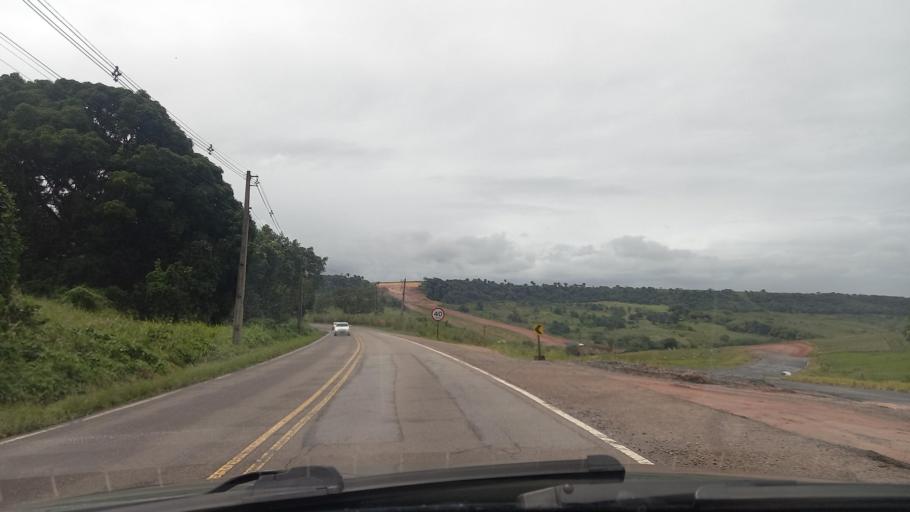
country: BR
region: Alagoas
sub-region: Sao Miguel Dos Campos
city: Sao Miguel dos Campos
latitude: -9.8211
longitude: -36.2213
